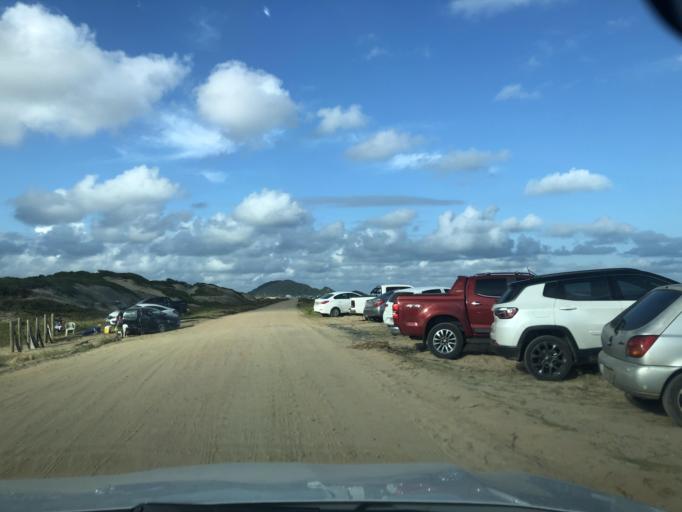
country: BR
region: Santa Catarina
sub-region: Sao Francisco Do Sul
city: Sao Francisco do Sul
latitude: -26.2531
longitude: -48.5146
